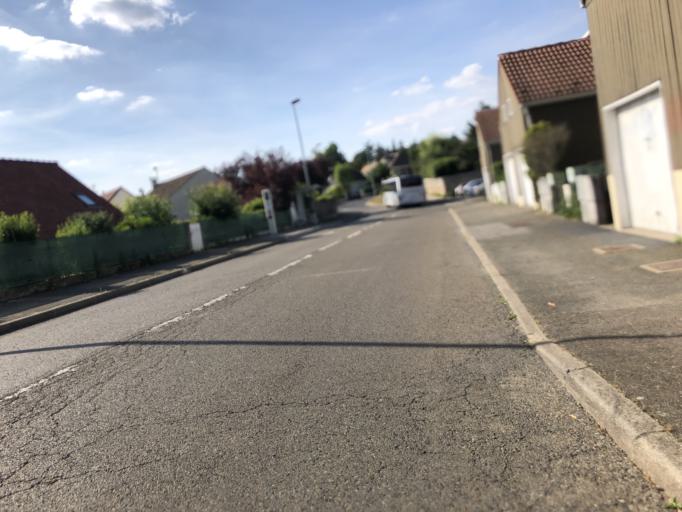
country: FR
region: Ile-de-France
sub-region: Departement des Yvelines
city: Triel-sur-Seine
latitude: 48.9777
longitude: 2.0142
